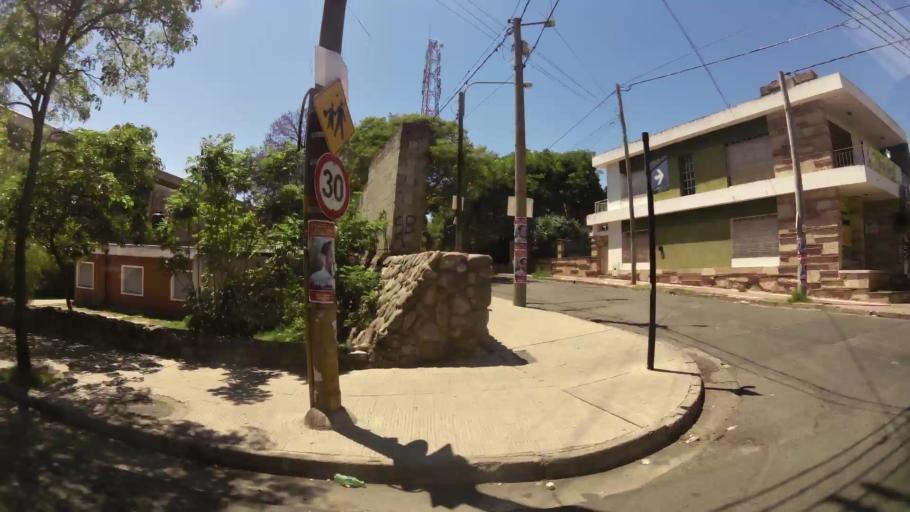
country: AR
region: Cordoba
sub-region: Departamento de Capital
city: Cordoba
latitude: -31.4194
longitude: -64.2002
